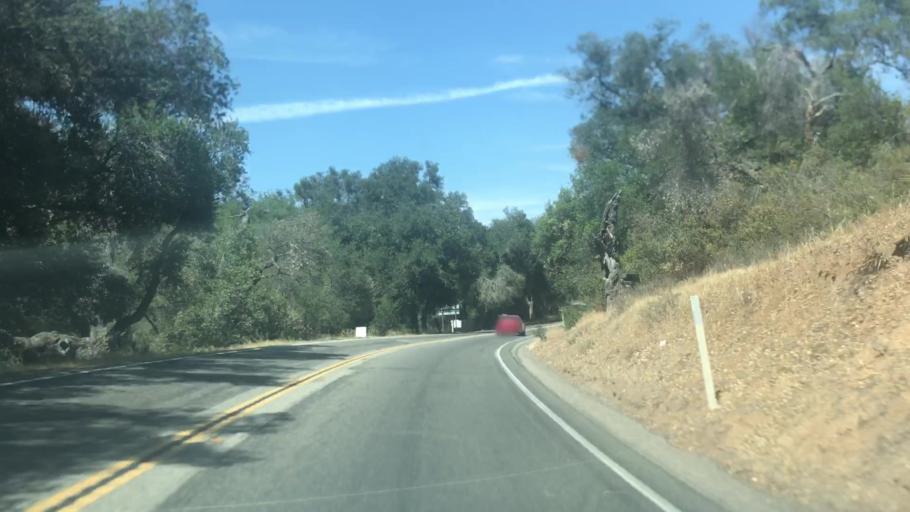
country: US
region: California
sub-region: Riverside County
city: Lakeland Village
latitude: 33.6496
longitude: -117.4160
